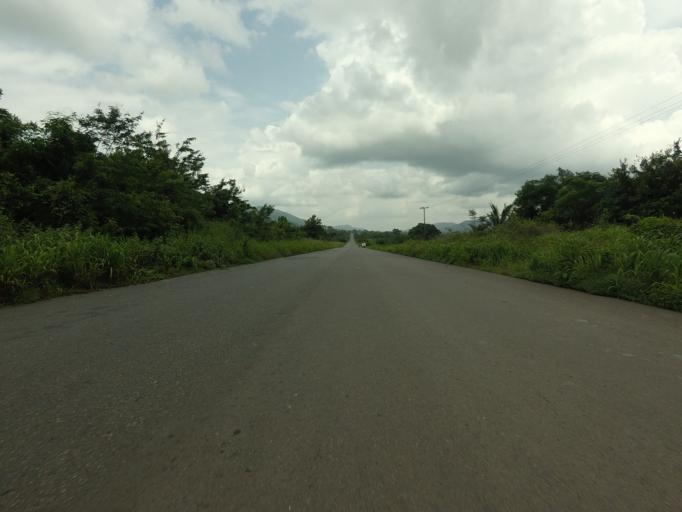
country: GH
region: Volta
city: Ho
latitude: 6.6181
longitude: 0.3053
